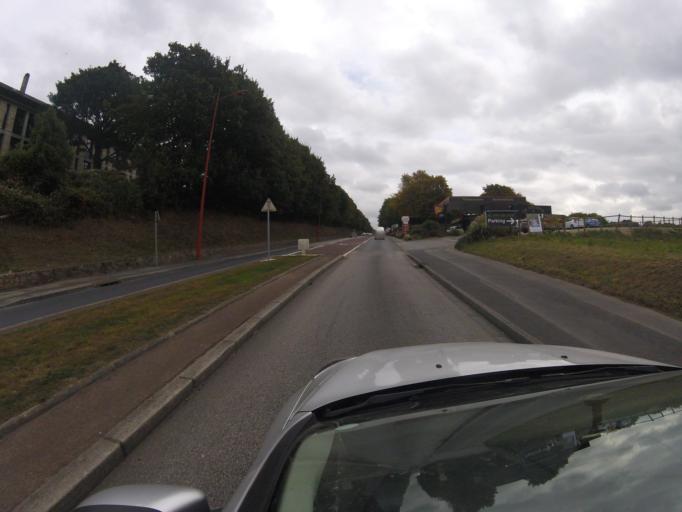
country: FR
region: Lower Normandy
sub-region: Departement de la Manche
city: Cherbourg-Octeville
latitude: 49.6191
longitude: -1.6115
